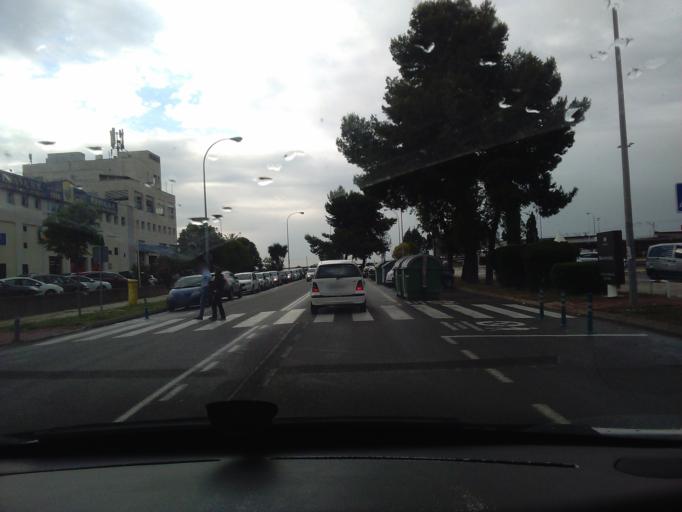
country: ES
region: Andalusia
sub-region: Provincia de Sevilla
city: Sevilla
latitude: 37.4086
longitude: -5.9408
